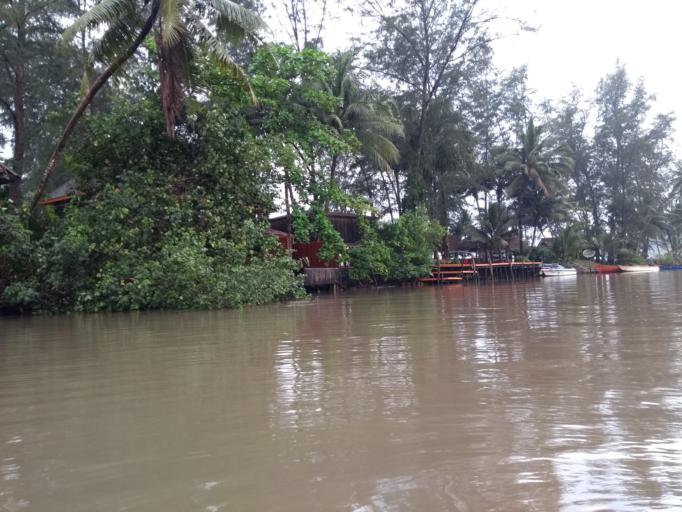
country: TH
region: Trat
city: Ko Kut
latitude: 11.6348
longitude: 102.5457
